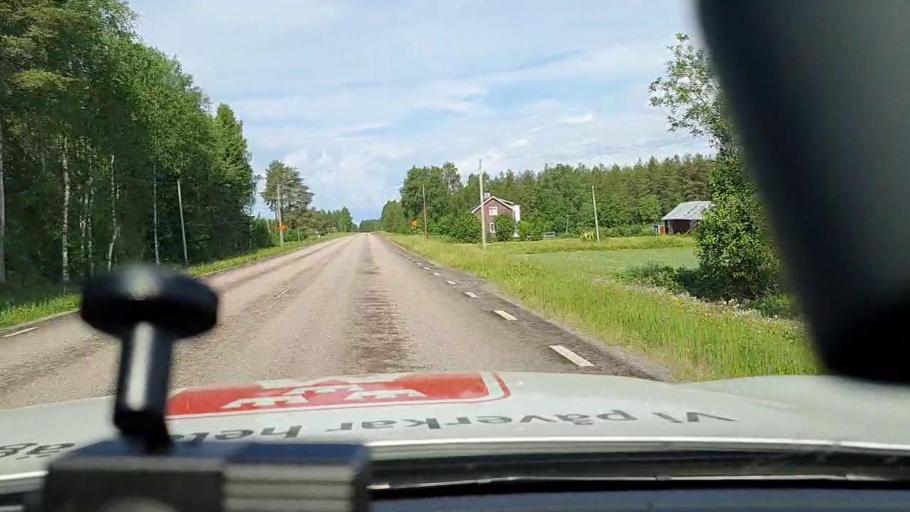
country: SE
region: Norrbotten
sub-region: Alvsbyns Kommun
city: AElvsbyn
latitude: 66.0175
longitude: 21.1509
